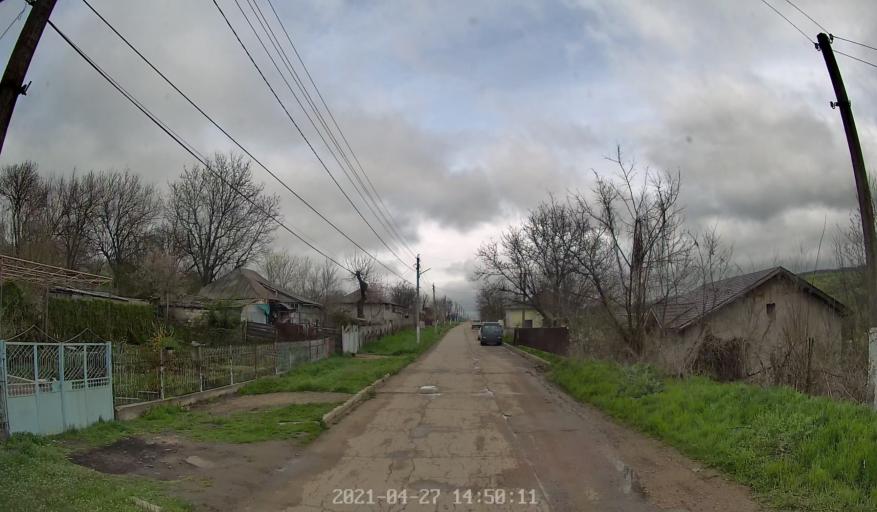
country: MD
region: Chisinau
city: Vadul lui Voda
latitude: 47.0477
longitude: 29.0570
